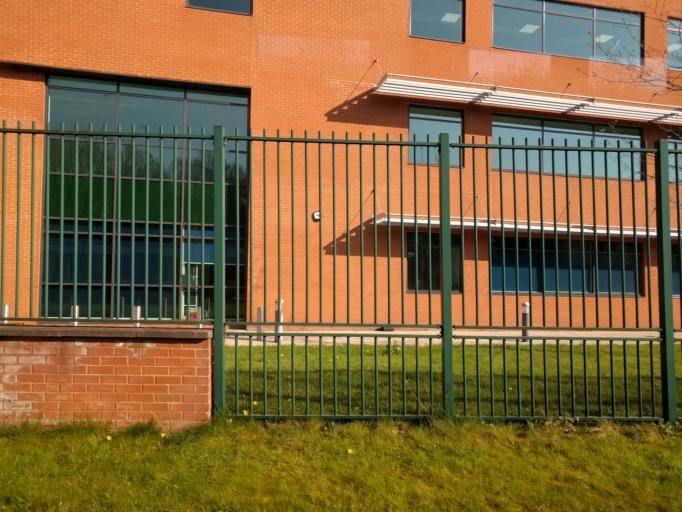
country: GB
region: England
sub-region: Manchester
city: Ringway
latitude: 53.3726
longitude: -2.2491
